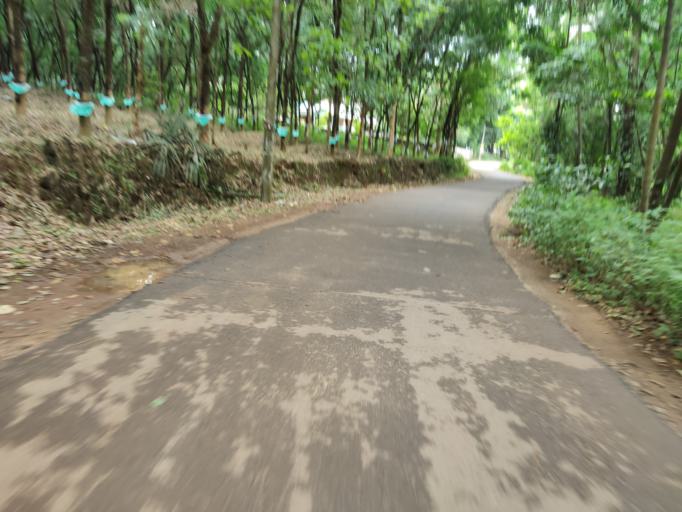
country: IN
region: Kerala
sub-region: Malappuram
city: Manjeri
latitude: 11.2222
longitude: 76.2535
